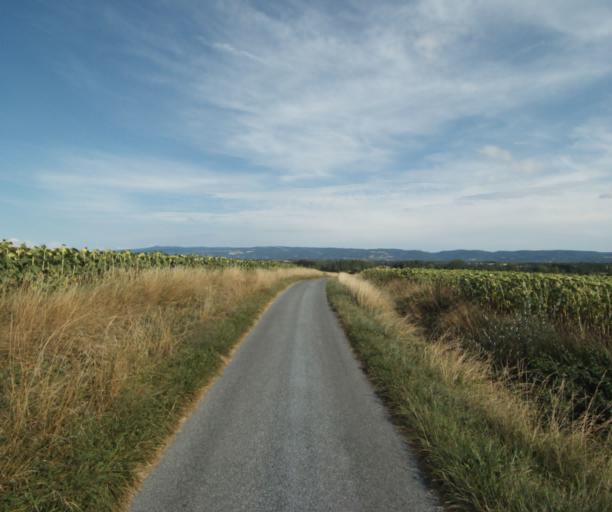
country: FR
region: Midi-Pyrenees
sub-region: Departement du Tarn
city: Puylaurens
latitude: 43.5300
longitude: 1.9918
